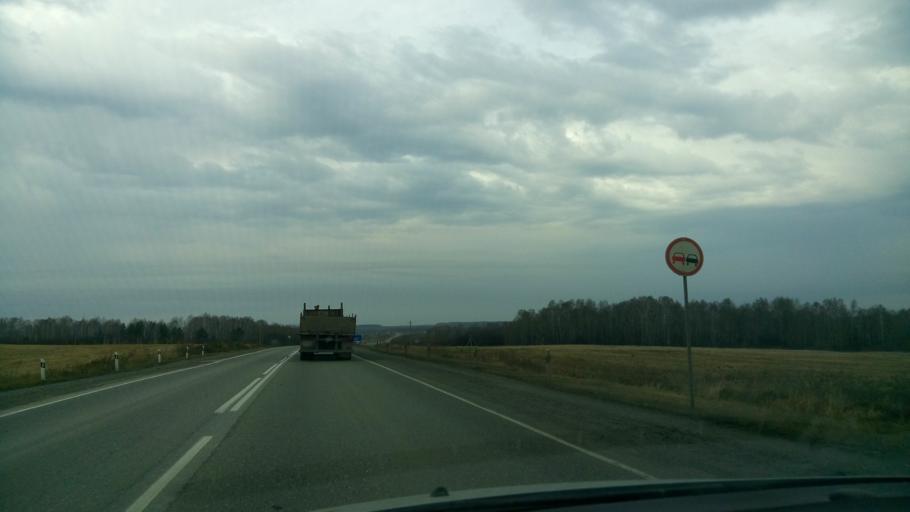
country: RU
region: Sverdlovsk
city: Kamyshlov
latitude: 56.8673
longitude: 62.7553
